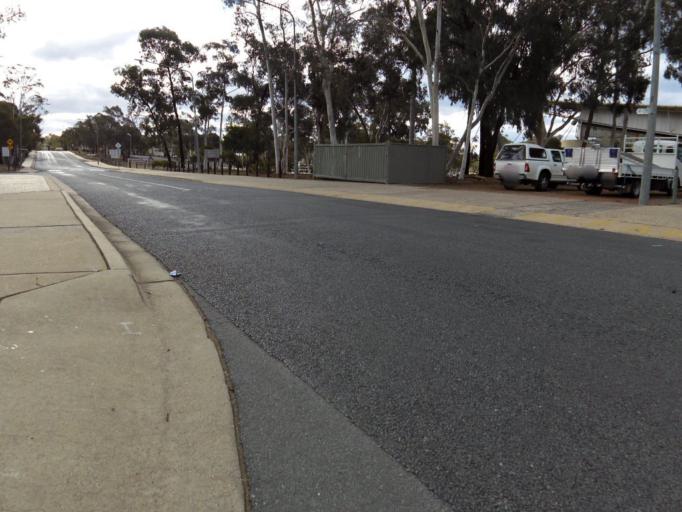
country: AU
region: Australian Capital Territory
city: Kaleen
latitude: -35.2487
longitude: 149.1005
